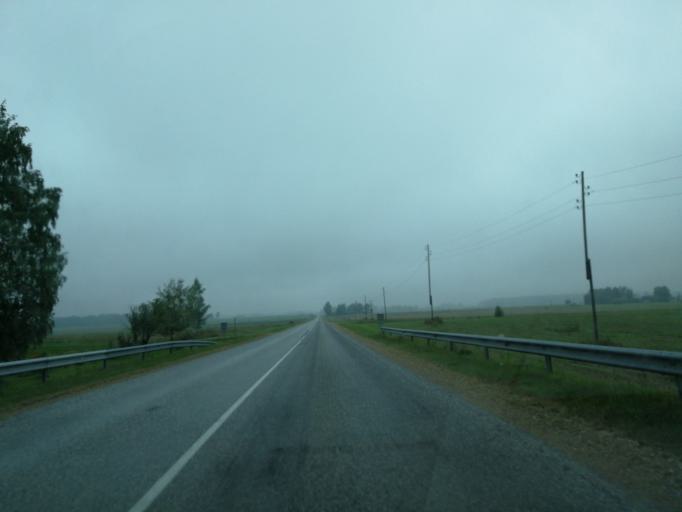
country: LV
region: Preilu Rajons
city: Preili
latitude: 56.3036
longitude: 26.6281
